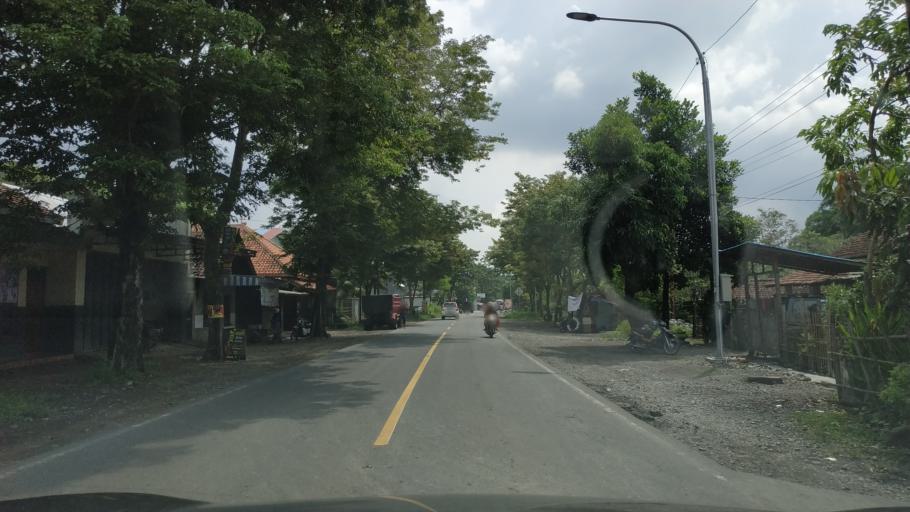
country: ID
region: Central Java
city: Lebaksiu
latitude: -7.0224
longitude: 109.1421
